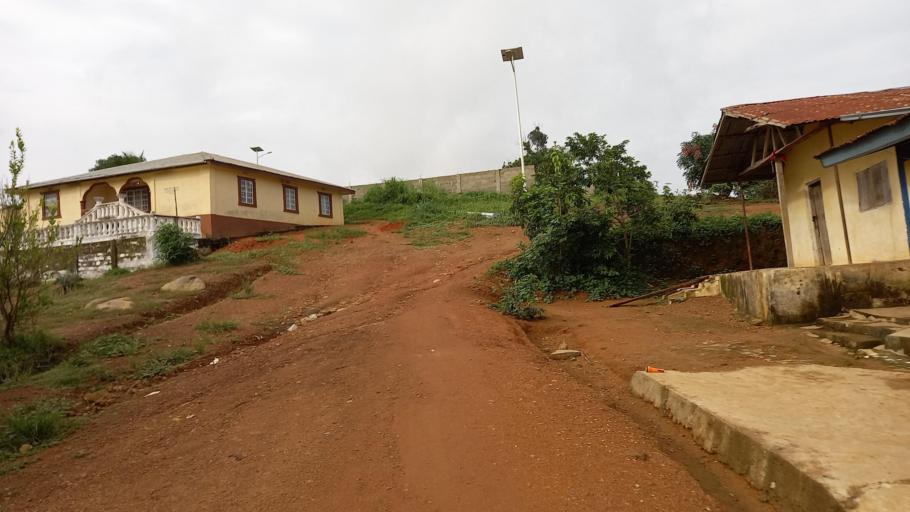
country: SL
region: Eastern Province
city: Kailahun
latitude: 8.2725
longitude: -10.5812
